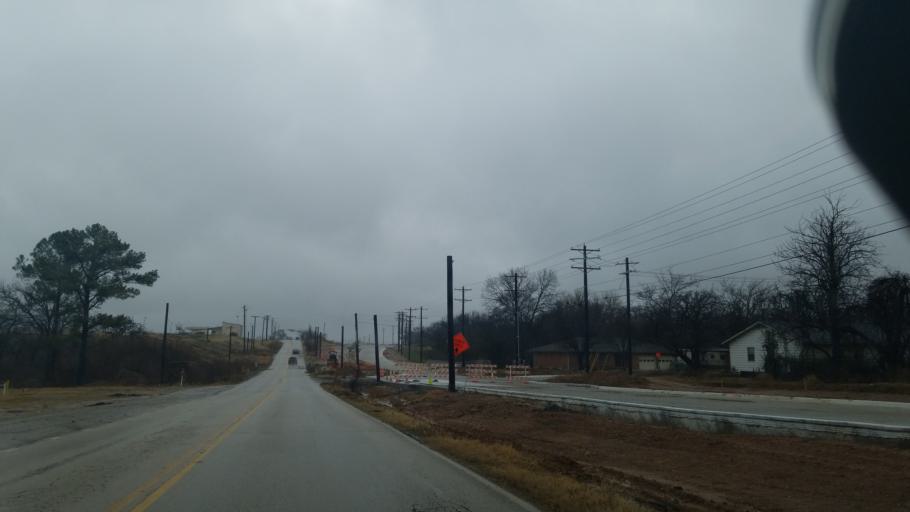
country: US
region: Texas
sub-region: Denton County
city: Corinth
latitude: 33.1990
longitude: -97.0845
